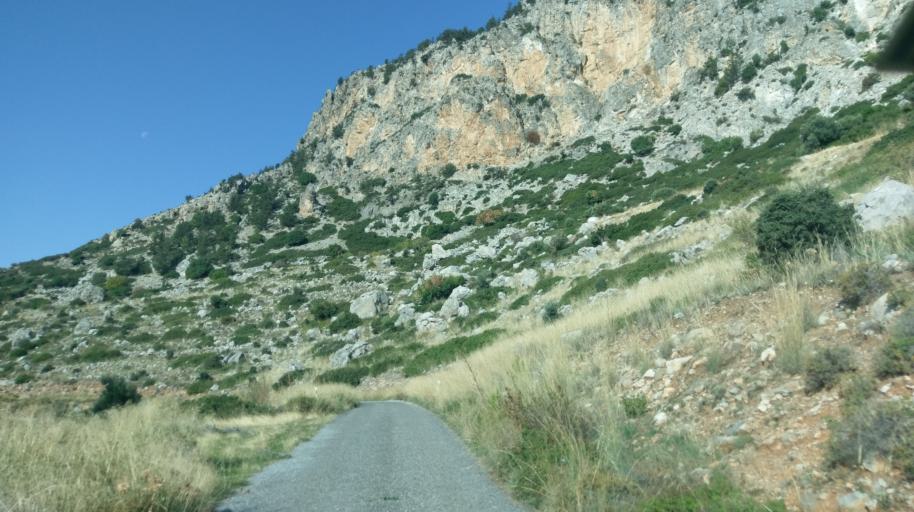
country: CY
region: Keryneia
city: Kyrenia
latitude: 35.2843
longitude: 33.4102
